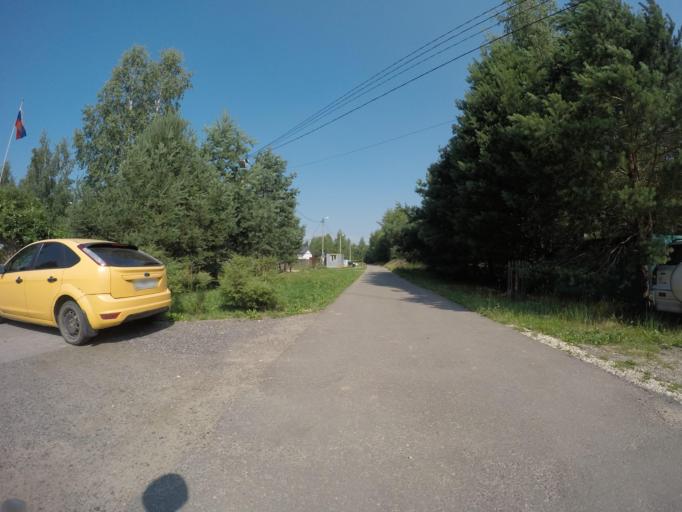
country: RU
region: Moskovskaya
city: Rechitsy
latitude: 55.6411
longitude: 38.5088
